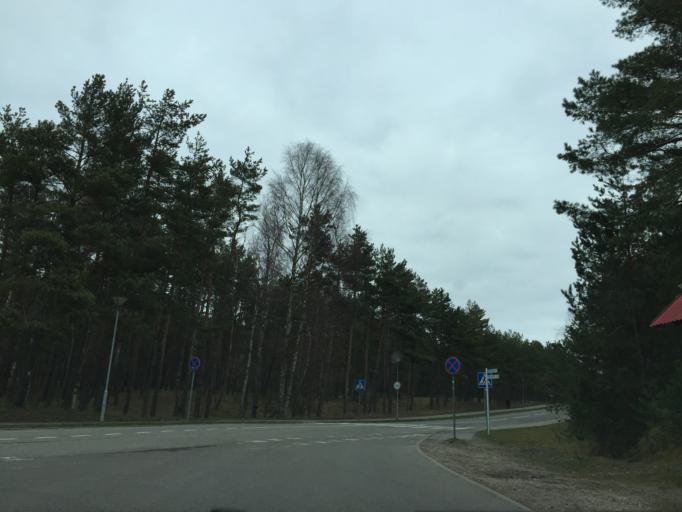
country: LT
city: Nida
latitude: 55.3014
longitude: 20.9909
